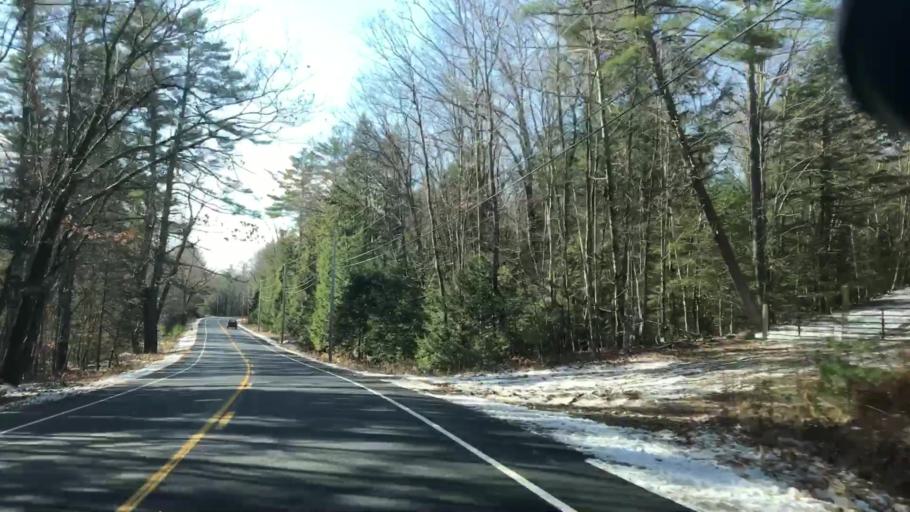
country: US
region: Maine
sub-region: Oxford County
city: Porter
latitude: 43.8001
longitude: -70.9158
